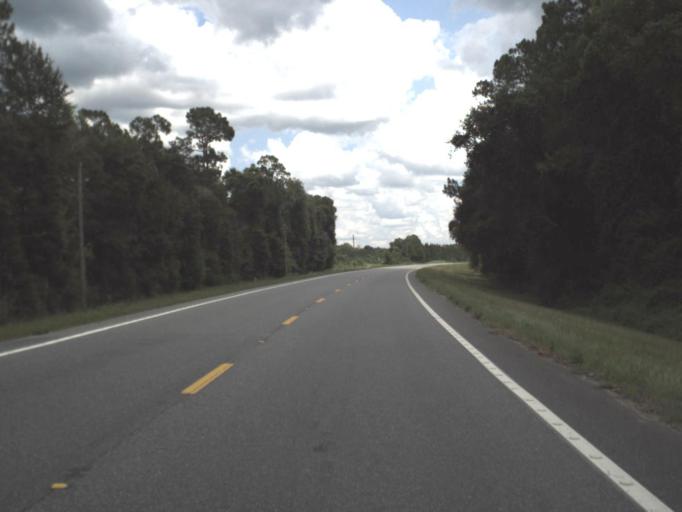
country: US
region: Florida
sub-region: Taylor County
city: Perry
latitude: 30.0932
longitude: -83.4904
